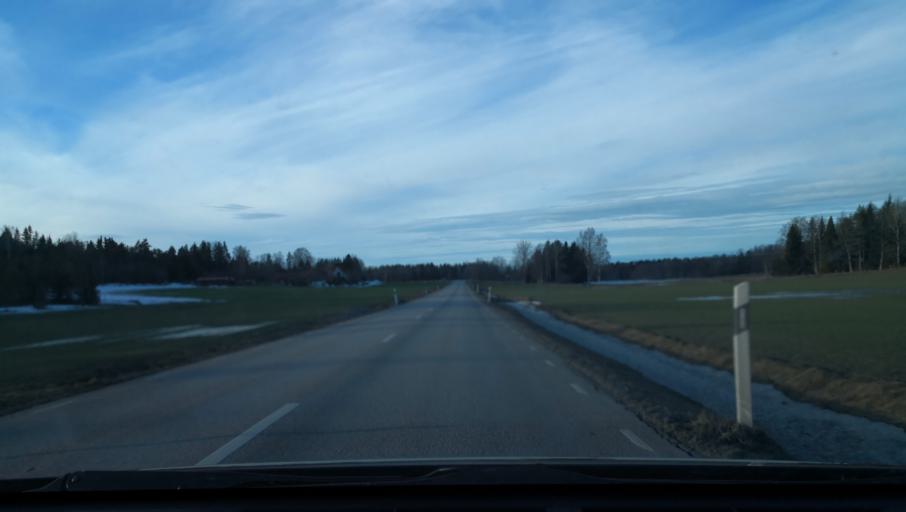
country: SE
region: Uppsala
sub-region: Osthammars Kommun
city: OEsthammar
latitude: 60.3030
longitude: 18.2748
